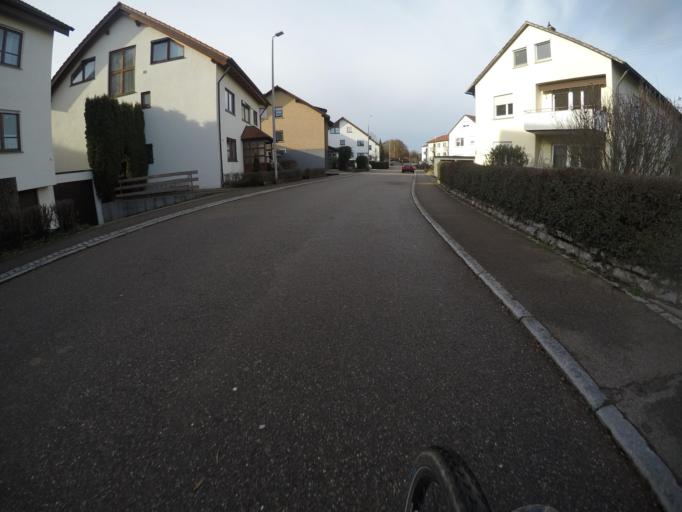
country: DE
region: Baden-Wuerttemberg
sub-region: Regierungsbezirk Stuttgart
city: Leutenbach
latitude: 48.8879
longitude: 9.3858
